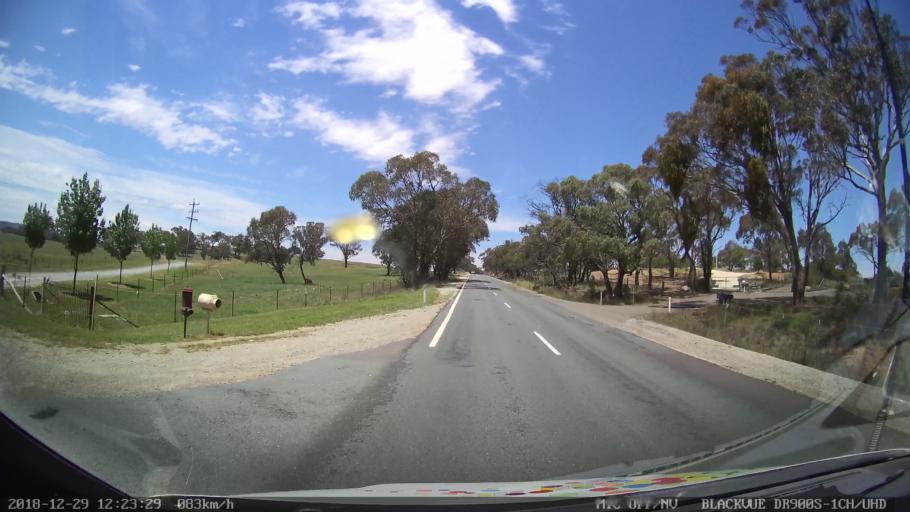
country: AU
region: New South Wales
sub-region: Queanbeyan
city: Queanbeyan
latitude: -35.4368
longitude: 149.2162
